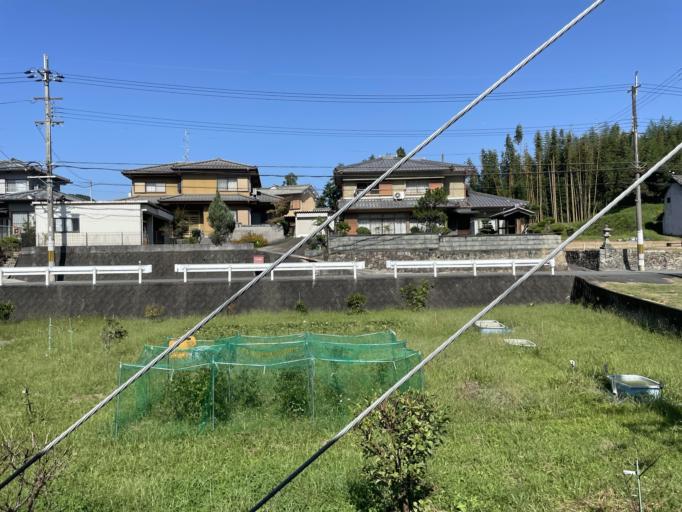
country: JP
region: Nara
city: Gose
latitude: 34.4389
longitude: 135.7679
